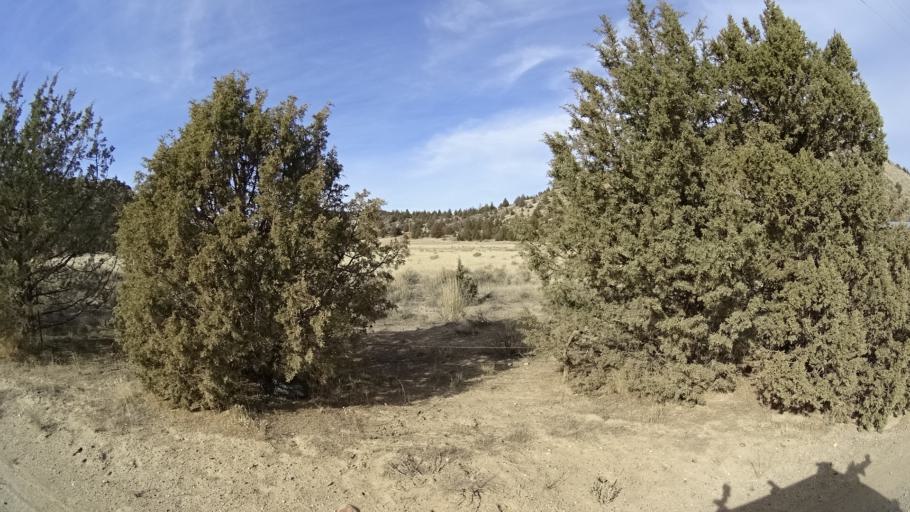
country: US
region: California
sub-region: Siskiyou County
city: Montague
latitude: 41.5811
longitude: -122.4550
